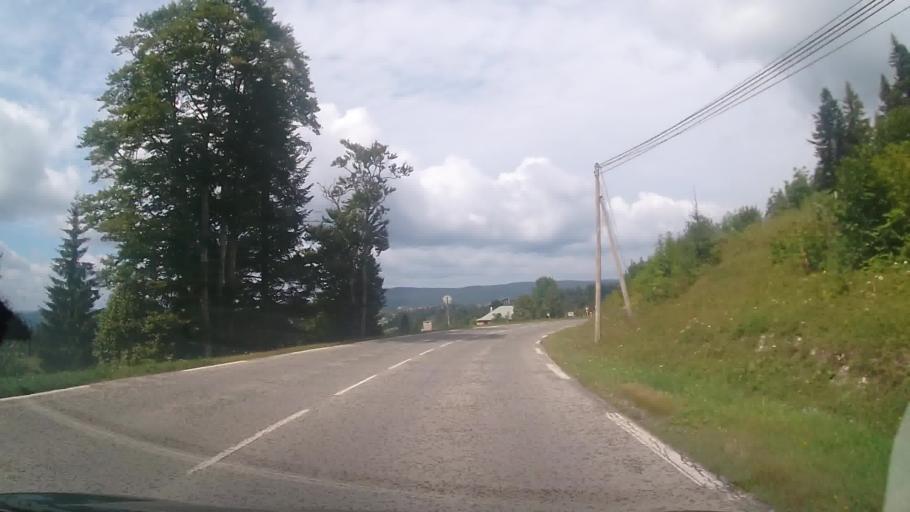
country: FR
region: Franche-Comte
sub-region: Departement du Jura
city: Les Rousses
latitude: 46.4525
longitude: 6.0709
